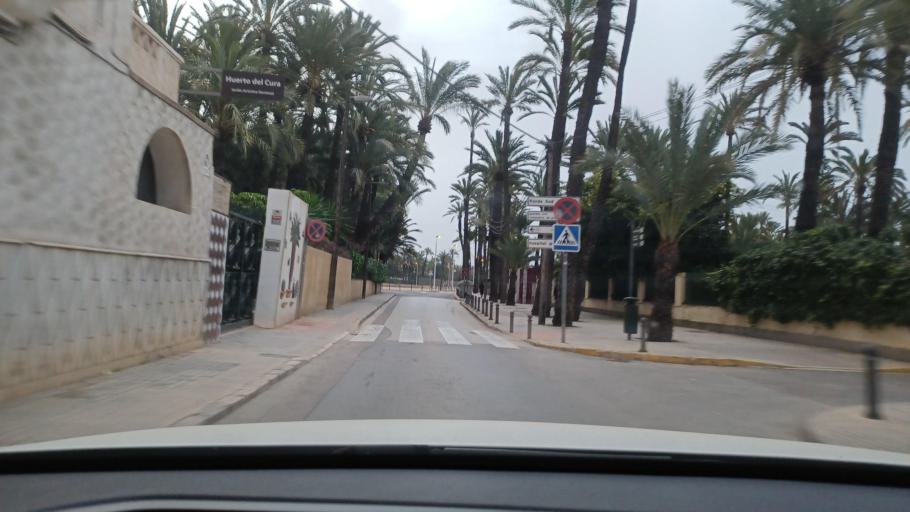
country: ES
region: Valencia
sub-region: Provincia de Alicante
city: Elche
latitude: 38.2639
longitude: -0.6919
